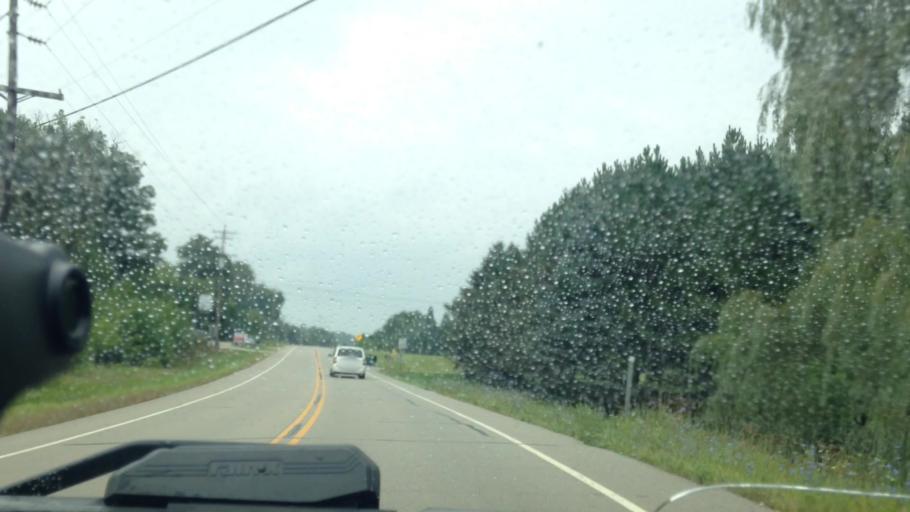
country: US
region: Wisconsin
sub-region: Washington County
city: Slinger
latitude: 43.3428
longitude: -88.3020
